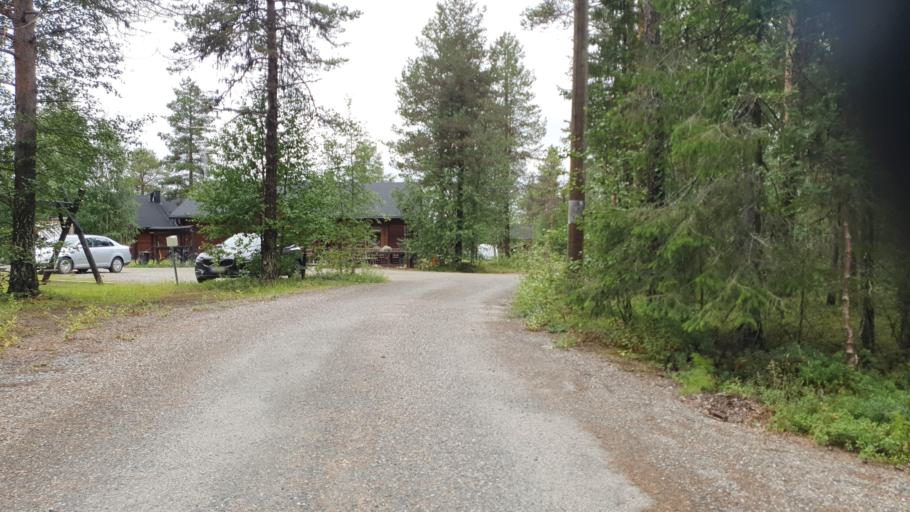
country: FI
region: Lapland
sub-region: Tunturi-Lappi
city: Kolari
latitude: 67.6129
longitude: 24.1392
